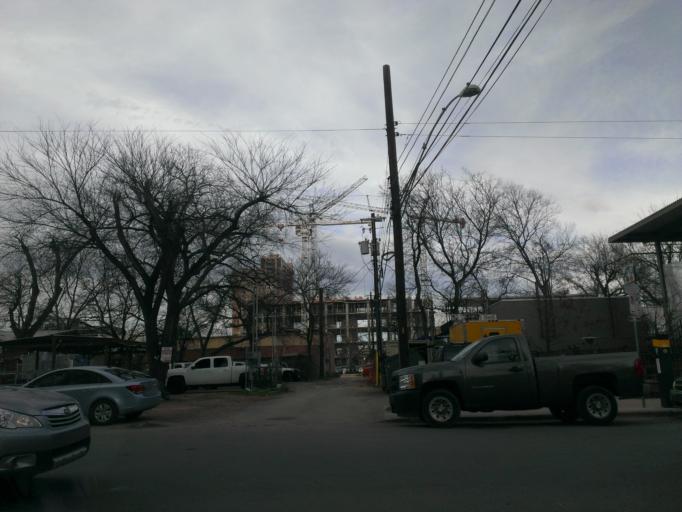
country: US
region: Texas
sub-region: Travis County
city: Austin
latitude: 30.2601
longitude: -97.7388
